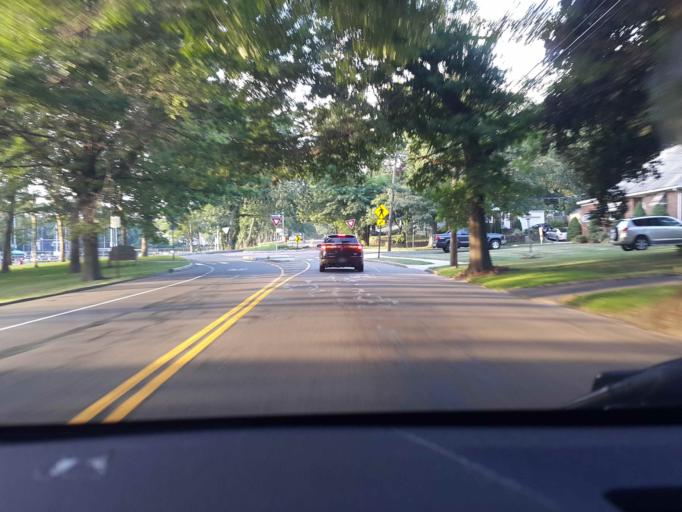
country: US
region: Connecticut
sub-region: New Haven County
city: East Haven
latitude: 41.2778
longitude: -72.8988
